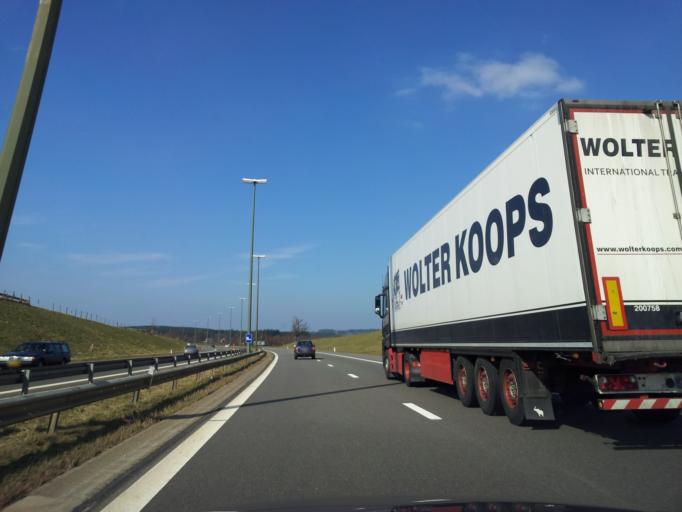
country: BE
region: Wallonia
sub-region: Province de Liege
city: Jalhay
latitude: 50.5185
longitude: 5.9441
